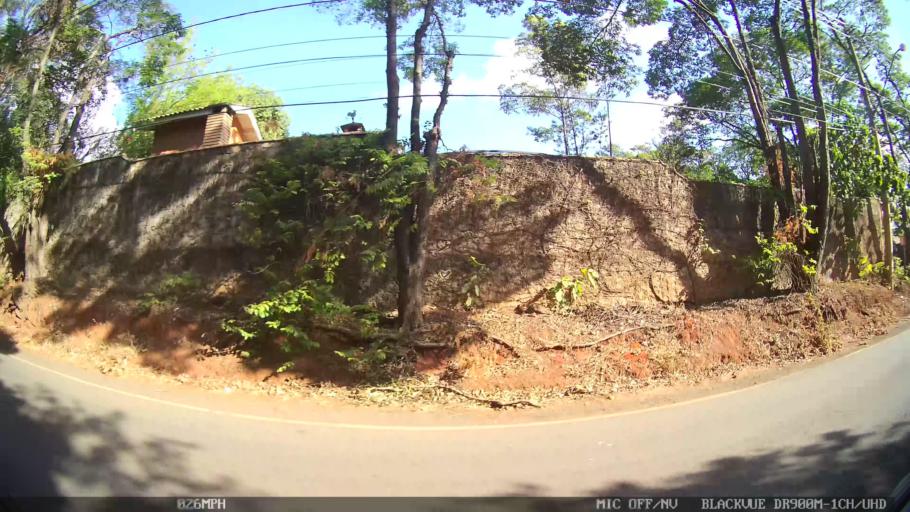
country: BR
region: Sao Paulo
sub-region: Nova Odessa
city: Nova Odessa
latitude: -22.8123
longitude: -47.3290
